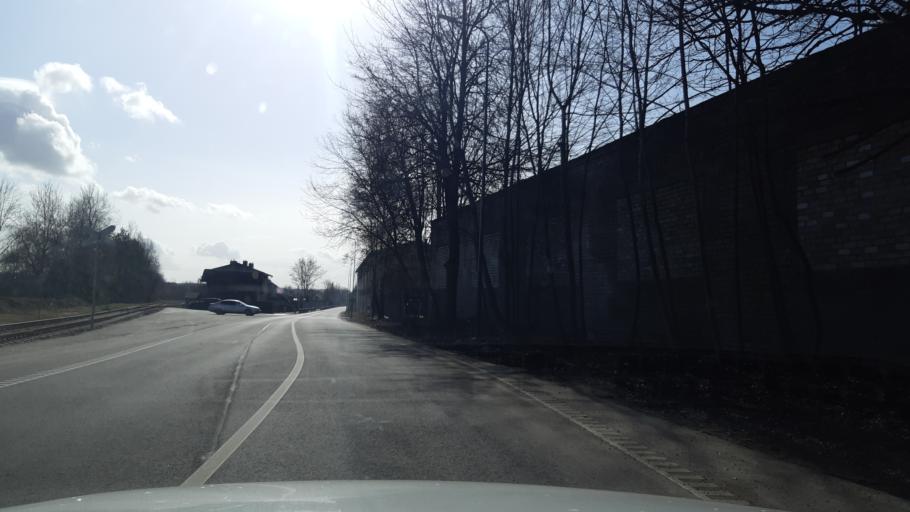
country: LT
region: Kauno apskritis
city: Dainava (Kaunas)
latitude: 54.8820
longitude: 23.9570
